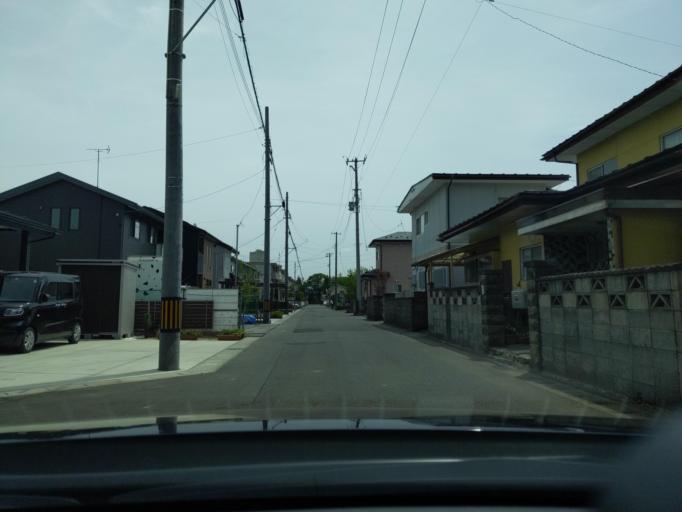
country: JP
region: Fukushima
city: Koriyama
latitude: 37.3950
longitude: 140.3136
